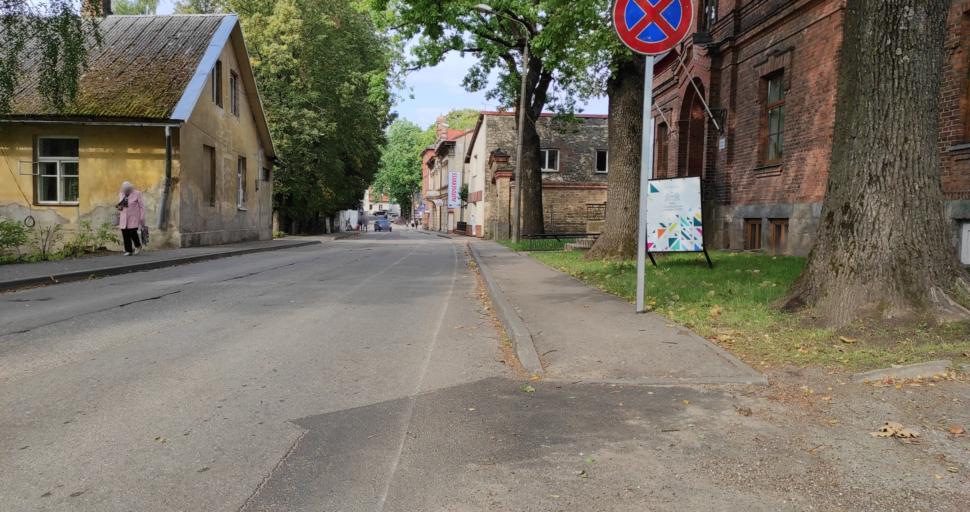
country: LV
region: Cesu Rajons
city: Cesis
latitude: 57.3107
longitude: 25.2746
